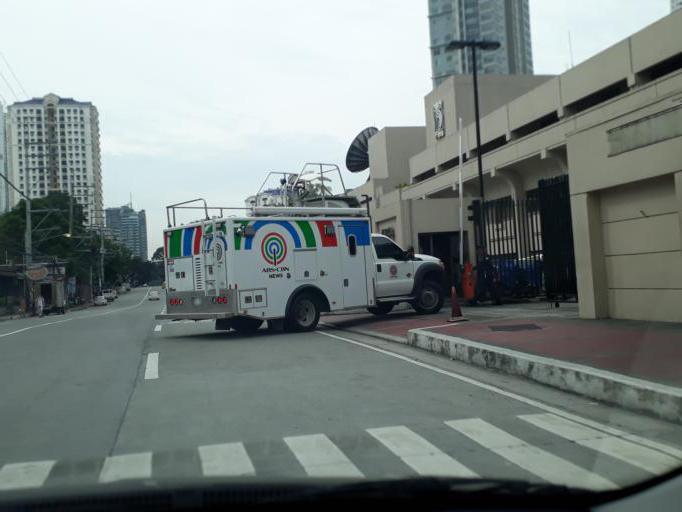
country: PH
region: Metro Manila
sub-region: Quezon City
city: Quezon City
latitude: 14.6405
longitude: 121.0371
